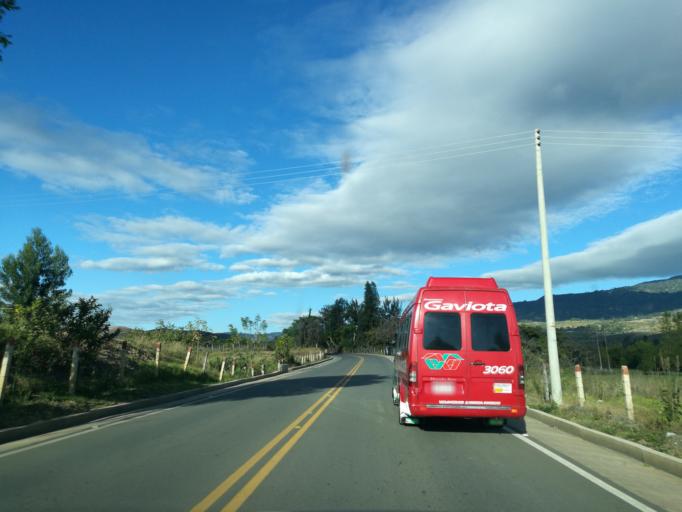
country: CO
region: Boyaca
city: Sutamarchan
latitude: 5.6199
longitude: -73.6094
